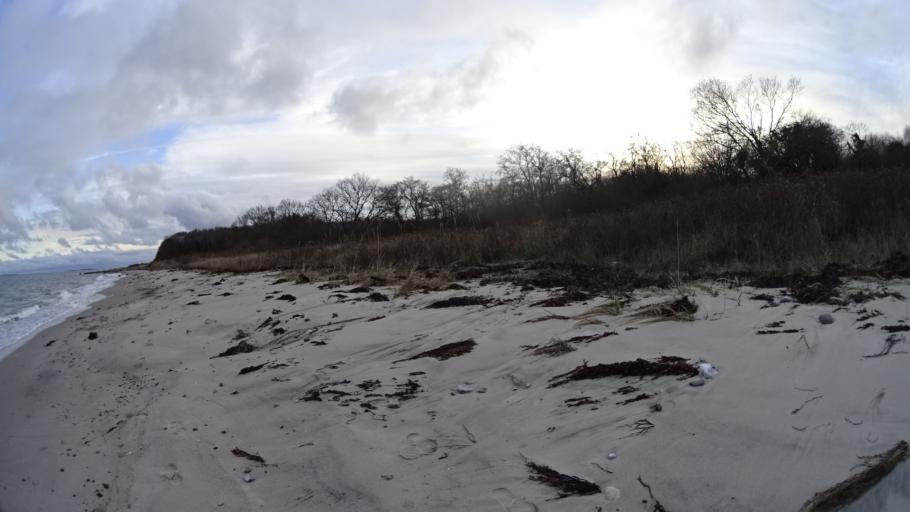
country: DK
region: Central Jutland
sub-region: Arhus Kommune
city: Beder
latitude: 56.0553
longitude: 10.2642
